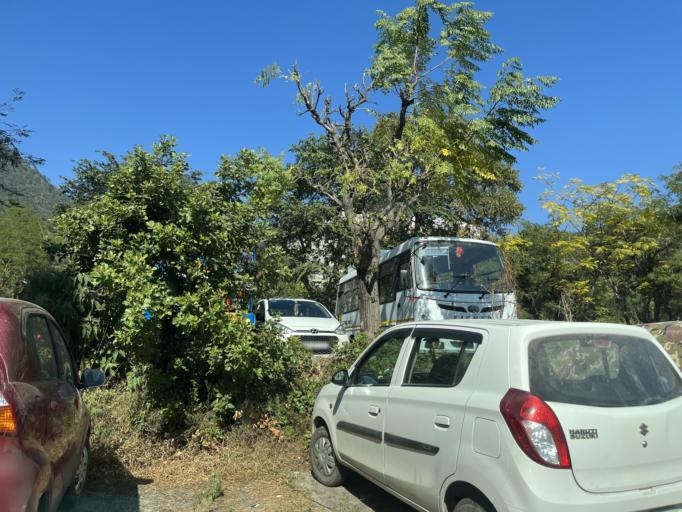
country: IN
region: Uttarakhand
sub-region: Almora
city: Ranikhet
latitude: 29.5550
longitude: 79.3400
